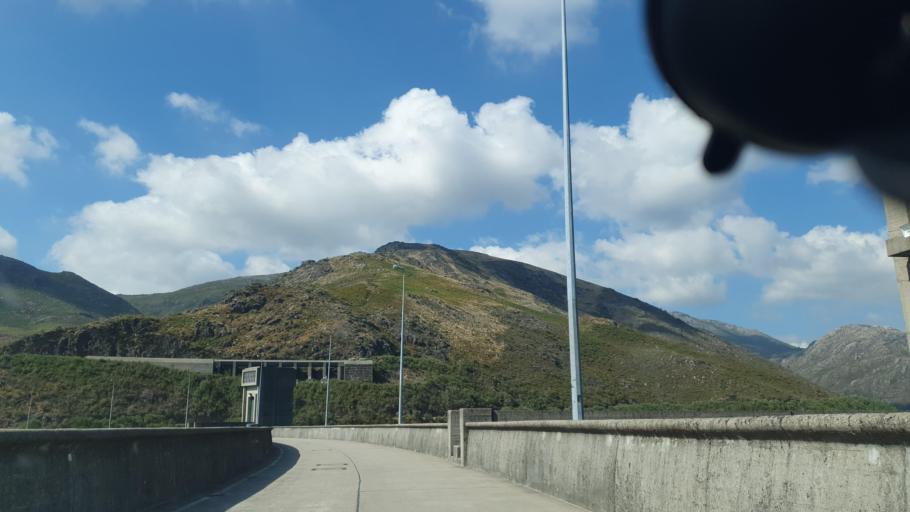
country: PT
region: Braga
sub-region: Terras de Bouro
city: Antas
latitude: 41.7628
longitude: -8.2086
